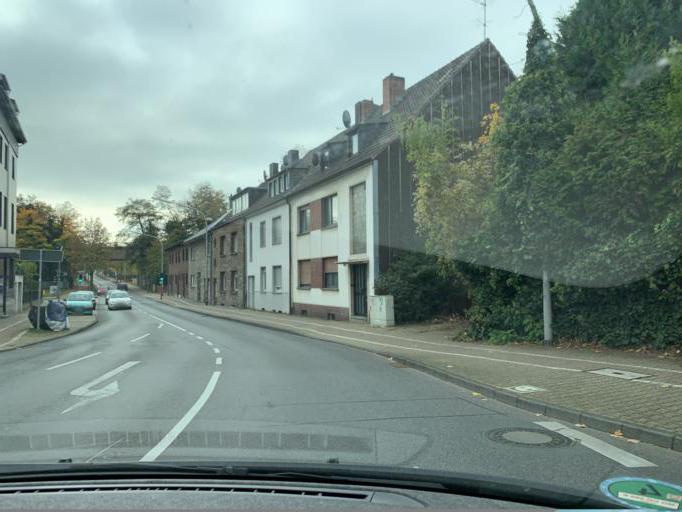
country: DE
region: North Rhine-Westphalia
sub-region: Regierungsbezirk Dusseldorf
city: Monchengladbach
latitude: 51.1577
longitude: 6.4419
